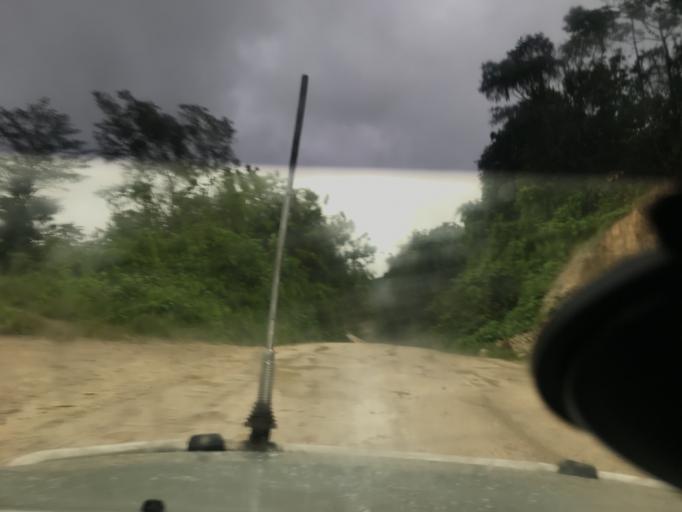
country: SB
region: Malaita
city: Auki
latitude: -9.0105
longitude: 160.8024
